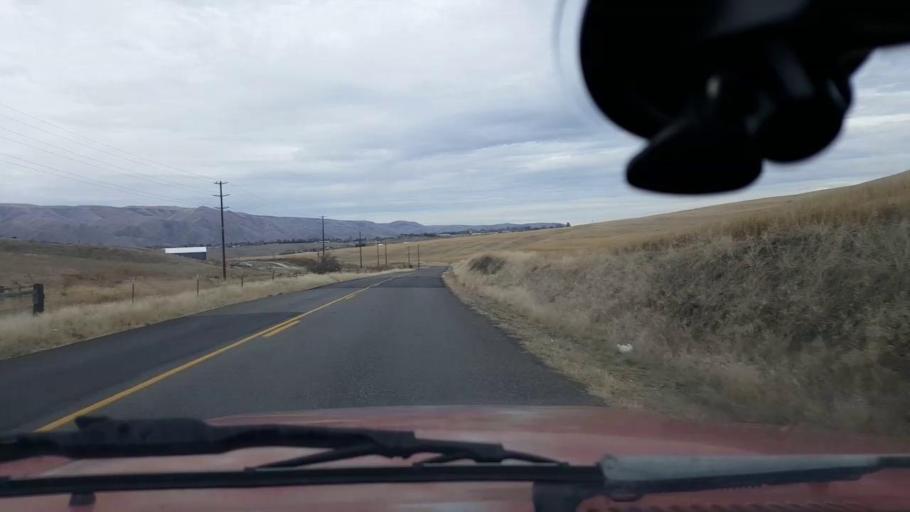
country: US
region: Washington
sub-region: Asotin County
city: Clarkston Heights-Vineland
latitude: 46.3873
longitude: -117.1117
